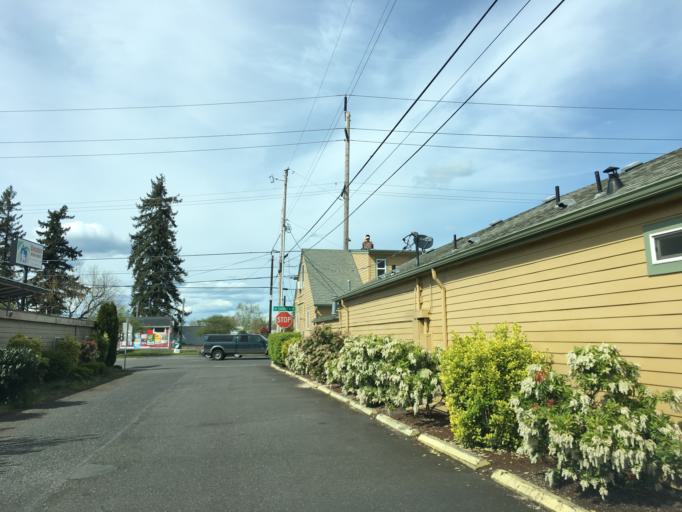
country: US
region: Oregon
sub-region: Multnomah County
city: Lents
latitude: 45.5570
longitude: -122.5399
